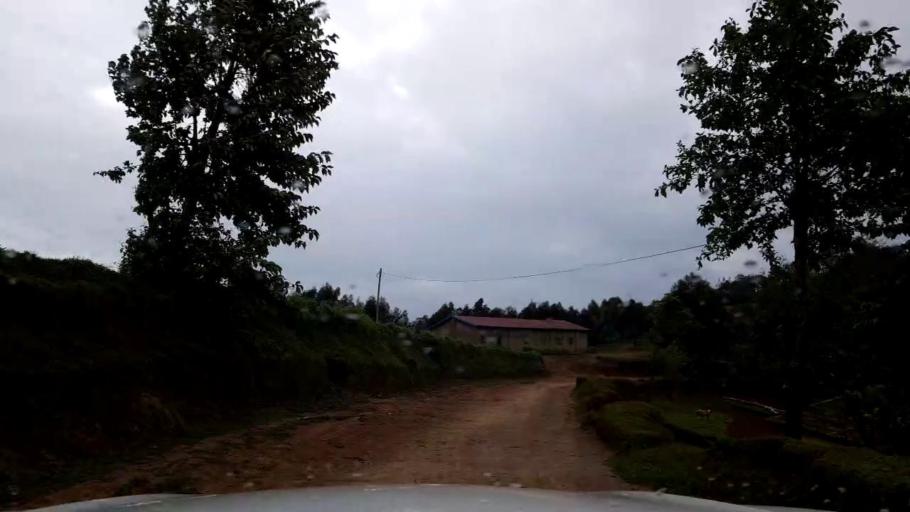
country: RW
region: Western Province
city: Kibuye
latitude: -2.0151
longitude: 29.4709
